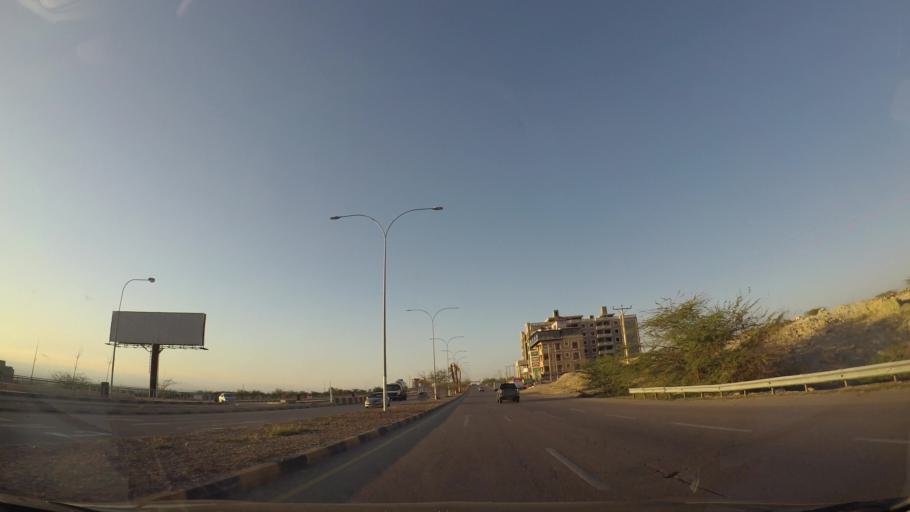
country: PS
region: West Bank
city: Jericho
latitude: 31.7506
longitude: 35.5948
